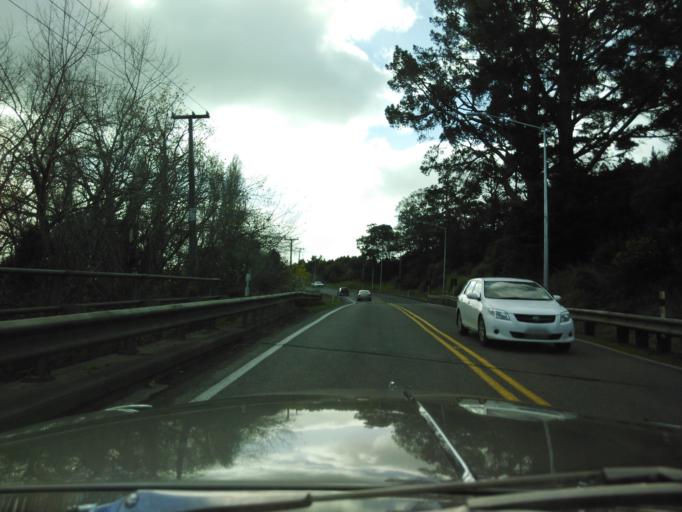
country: NZ
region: Auckland
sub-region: Auckland
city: Wellsford
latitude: -36.2513
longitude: 174.5091
